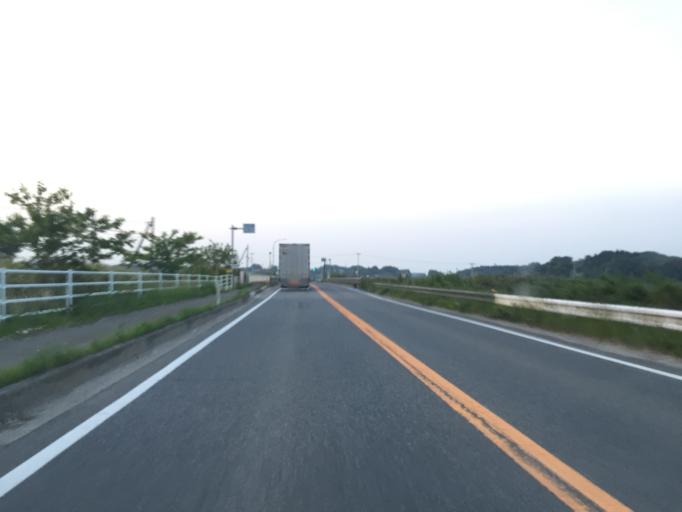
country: JP
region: Fukushima
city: Namie
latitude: 37.5957
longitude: 141.0032
